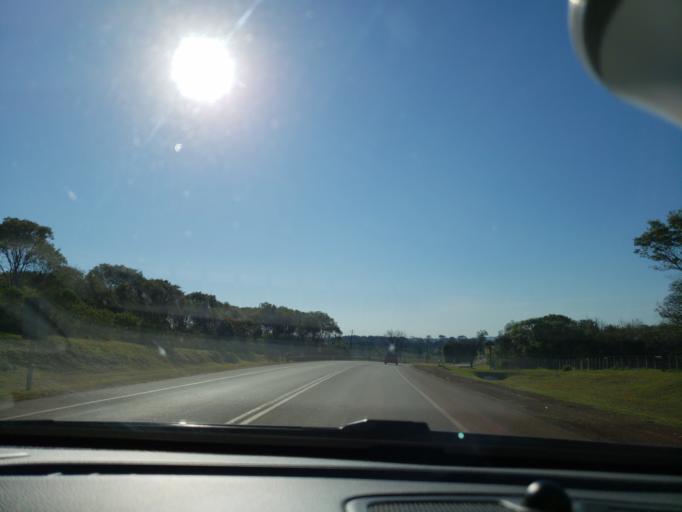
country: AR
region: Misiones
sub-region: Departamento de Apostoles
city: San Jose
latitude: -27.7977
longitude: -55.7705
